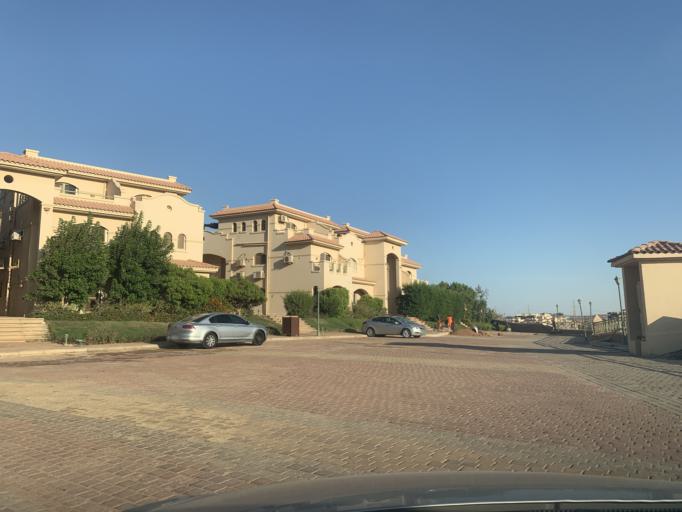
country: EG
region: As Suways
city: Ain Sukhna
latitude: 29.3716
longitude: 32.5691
